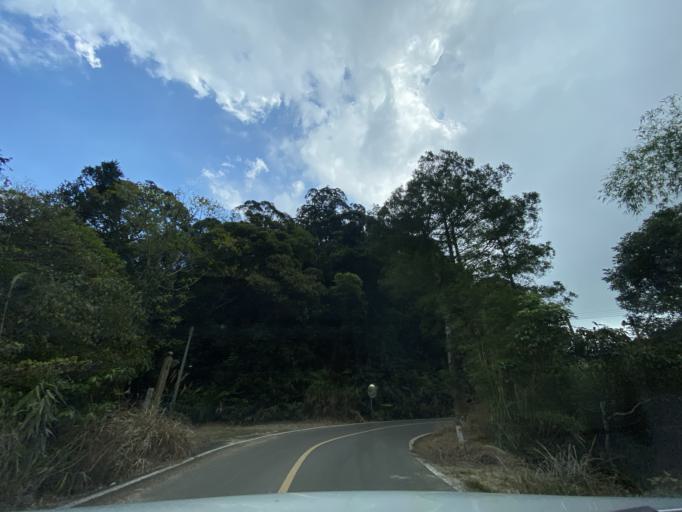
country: CN
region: Hainan
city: Diaoluoshan
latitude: 18.7233
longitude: 109.8696
